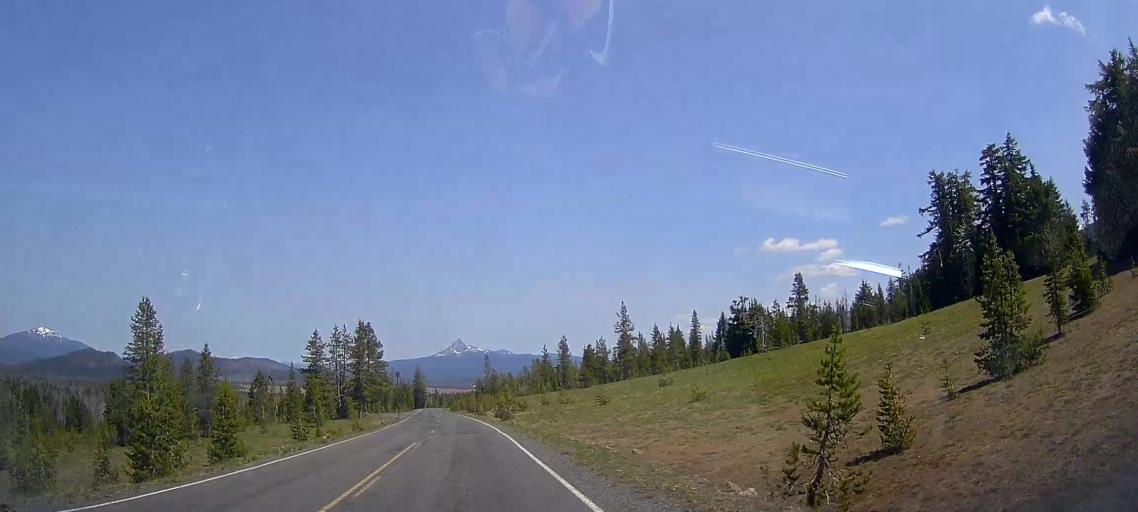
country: US
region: Oregon
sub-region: Jackson County
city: Shady Cove
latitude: 42.9892
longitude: -122.1438
